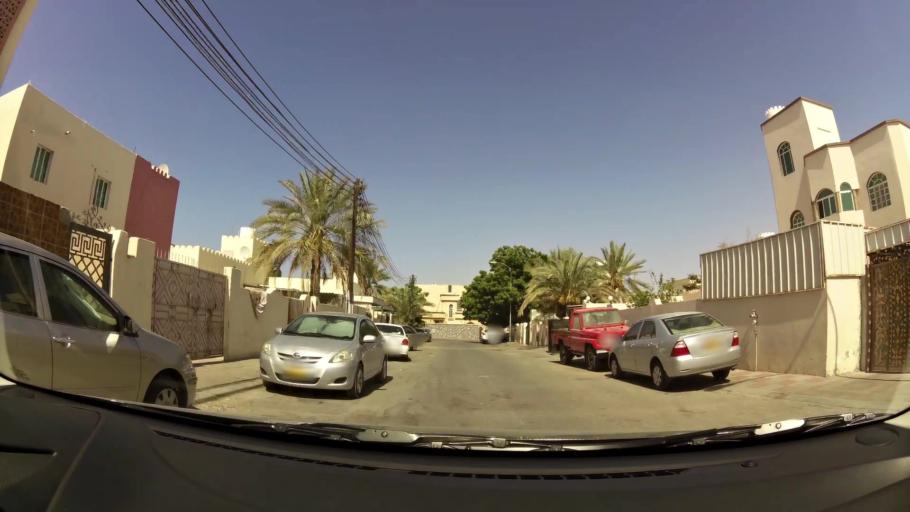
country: OM
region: Muhafazat Masqat
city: Bawshar
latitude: 23.6027
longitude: 58.3814
